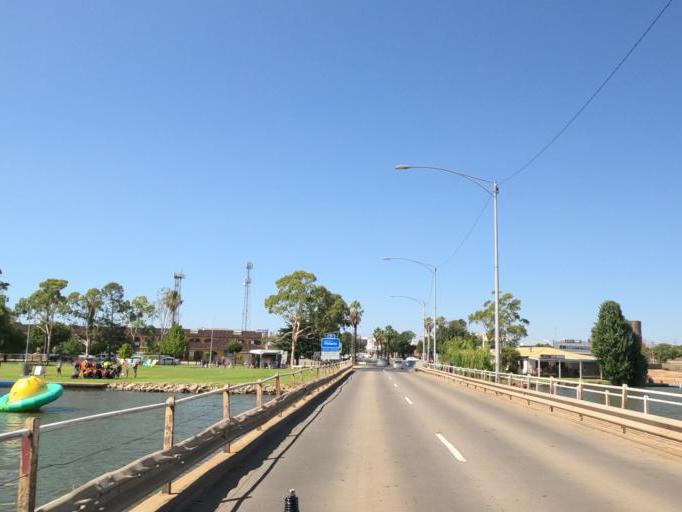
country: AU
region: Victoria
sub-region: Moira
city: Yarrawonga
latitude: -36.0069
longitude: 146.0050
